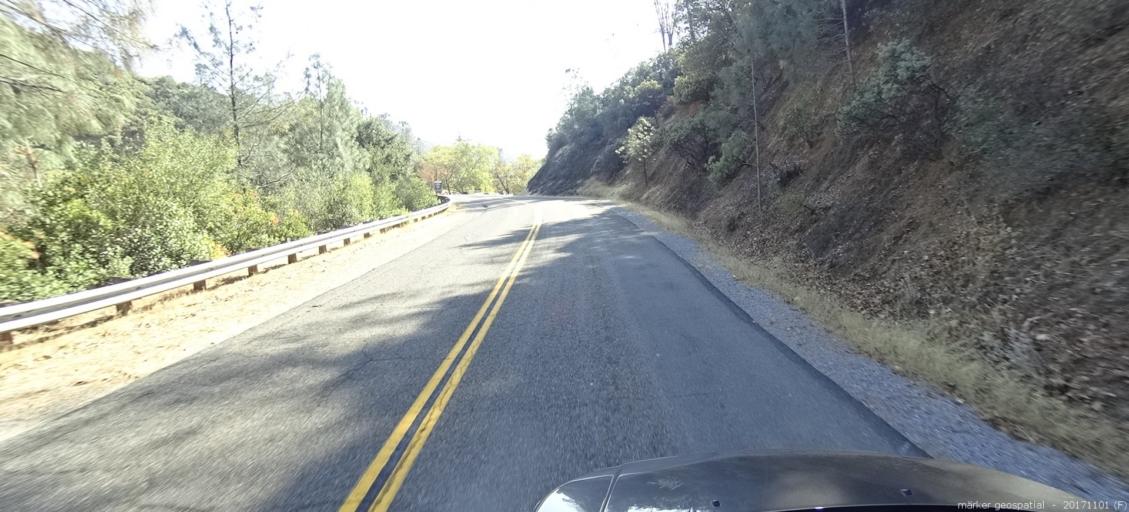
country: US
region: California
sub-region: Shasta County
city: Central Valley (historical)
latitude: 40.7139
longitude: -122.4074
